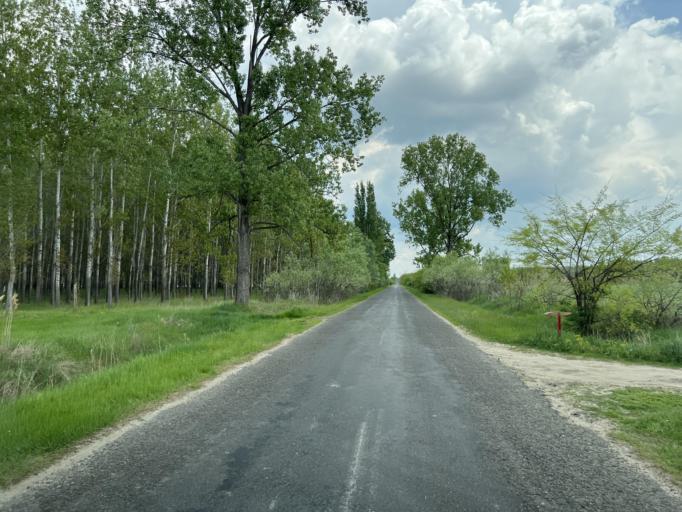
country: HU
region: Pest
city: Nagykoros
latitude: 47.0944
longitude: 19.7549
